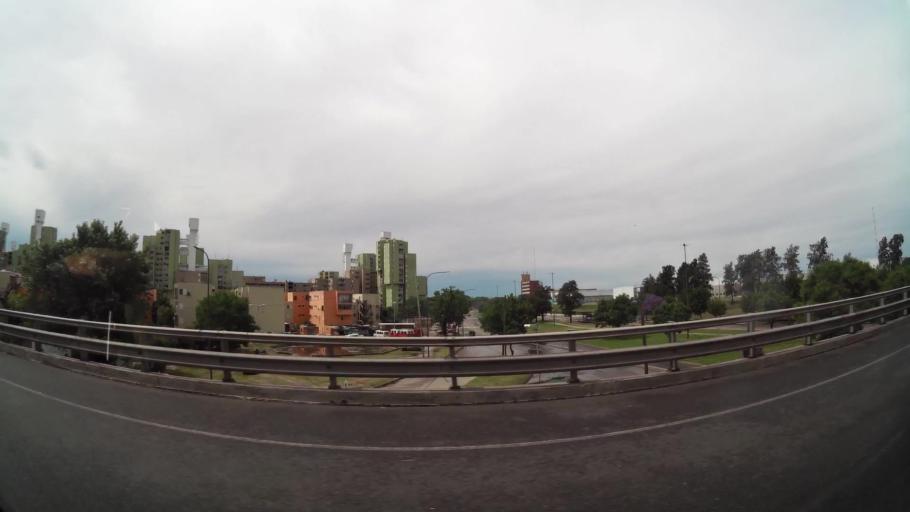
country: AR
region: Buenos Aires F.D.
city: Villa Lugano
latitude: -34.6696
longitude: -58.4444
